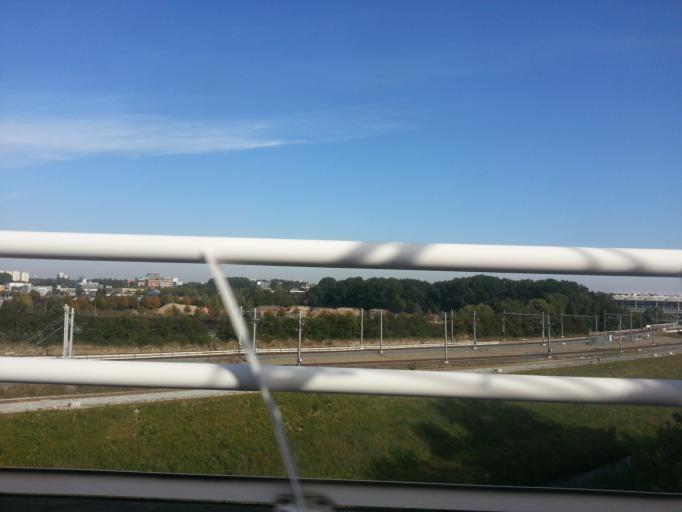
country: NL
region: North Holland
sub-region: Gemeente Ouder-Amstel
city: Duivendrecht
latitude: 52.3213
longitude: 4.9319
